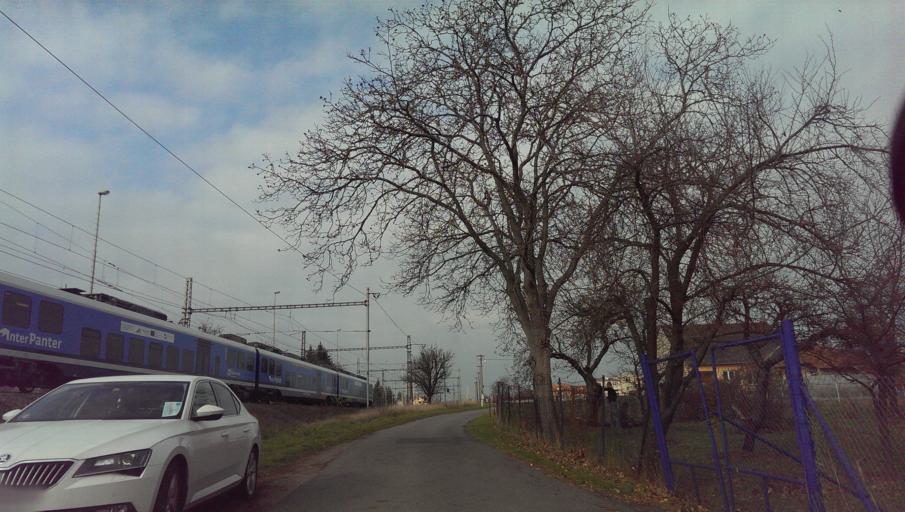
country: CZ
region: Zlin
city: Tlumacov
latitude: 49.2491
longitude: 17.5039
